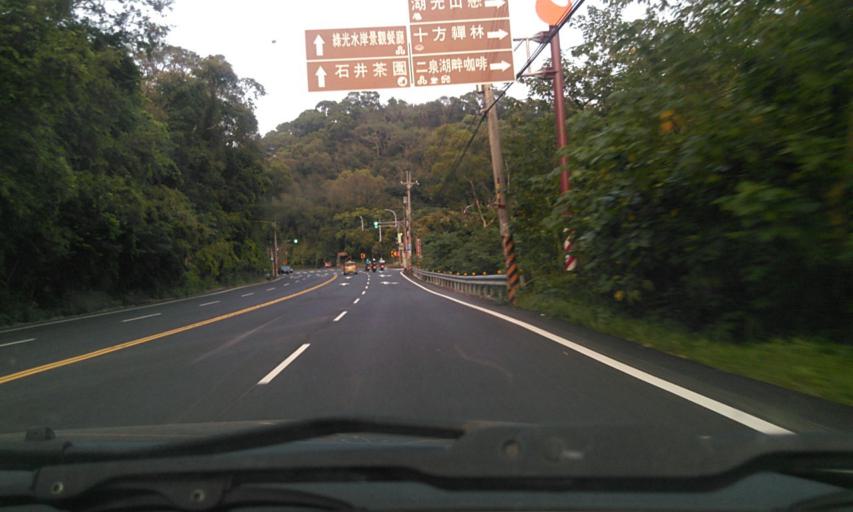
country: TW
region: Taiwan
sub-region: Hsinchu
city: Hsinchu
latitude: 24.6886
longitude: 120.9748
